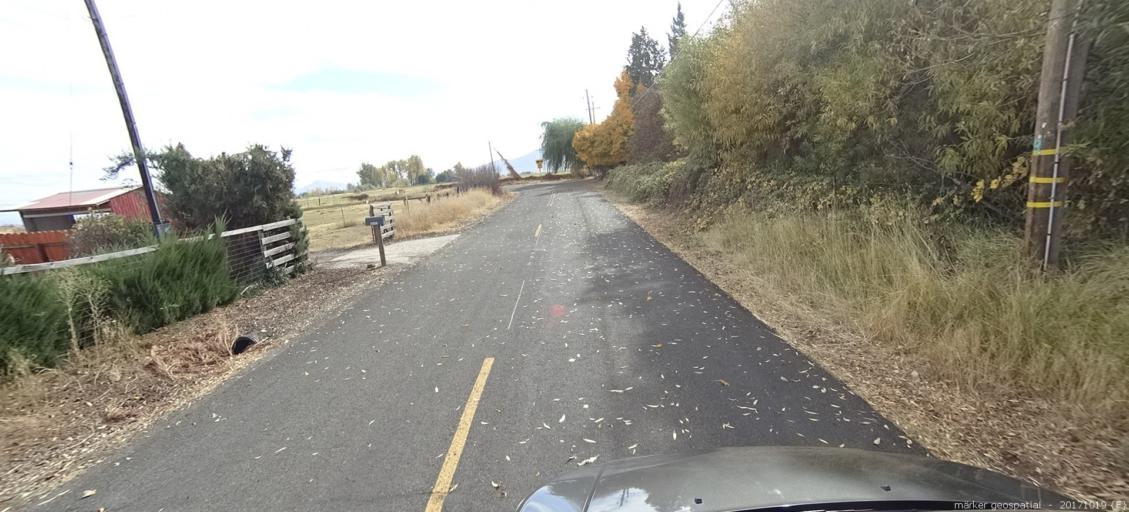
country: US
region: California
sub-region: Shasta County
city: Burney
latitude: 41.1037
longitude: -121.4951
